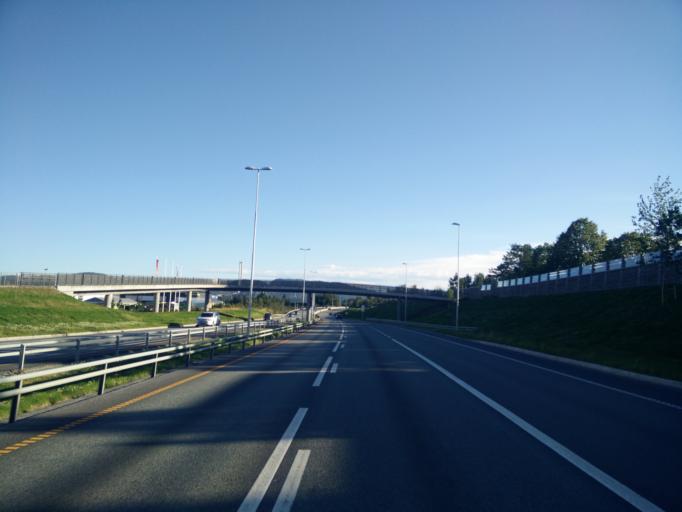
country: NO
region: Sor-Trondelag
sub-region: Trondheim
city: Trondheim
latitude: 63.3572
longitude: 10.3713
